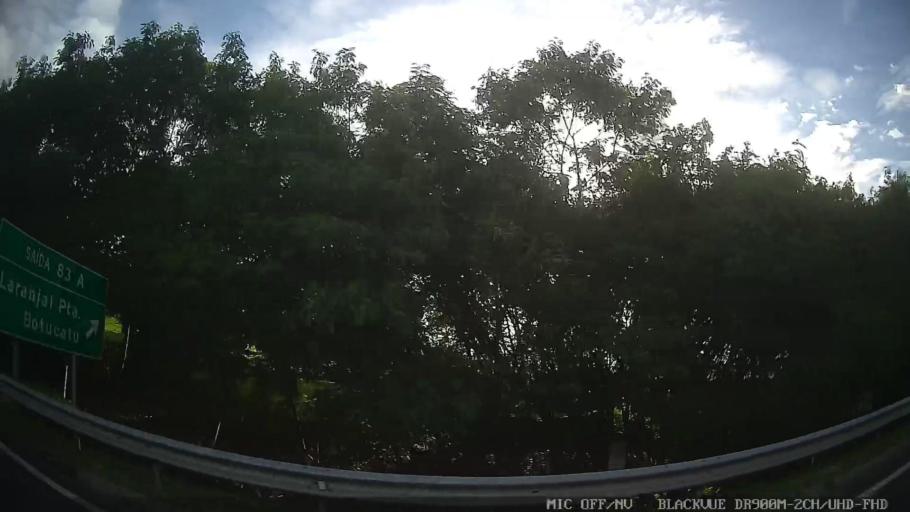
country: BR
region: Sao Paulo
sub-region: Tiete
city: Tiete
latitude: -23.1153
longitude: -47.7189
